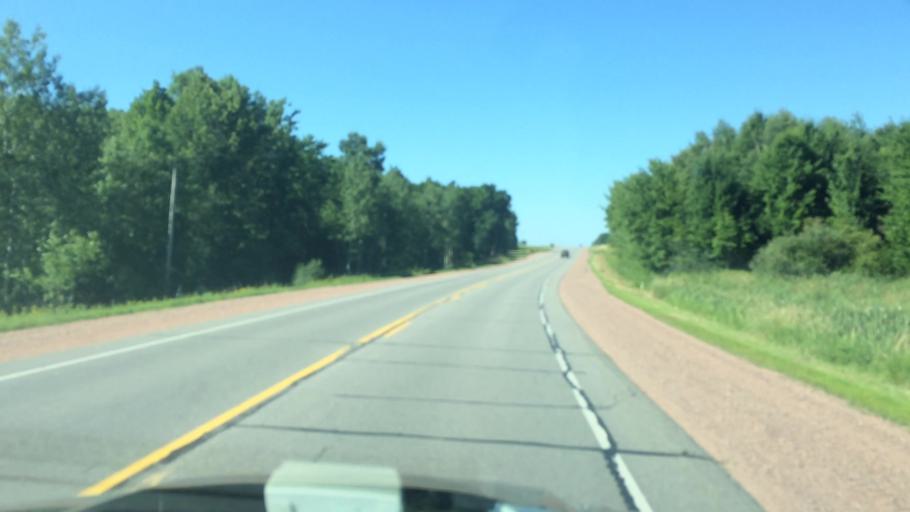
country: US
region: Wisconsin
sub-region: Marathon County
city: Stratford
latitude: 44.7346
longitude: -90.0812
